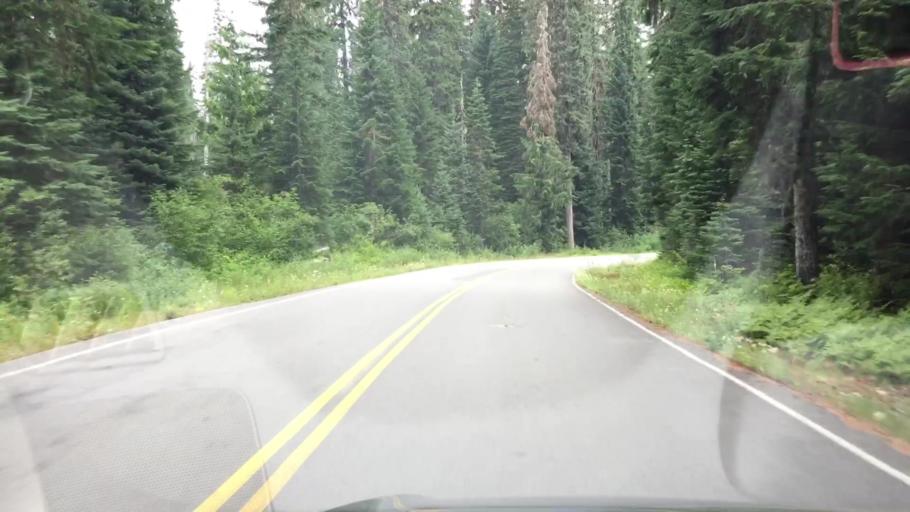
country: US
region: Washington
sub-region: Klickitat County
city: White Salmon
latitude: 46.1619
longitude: -121.6318
